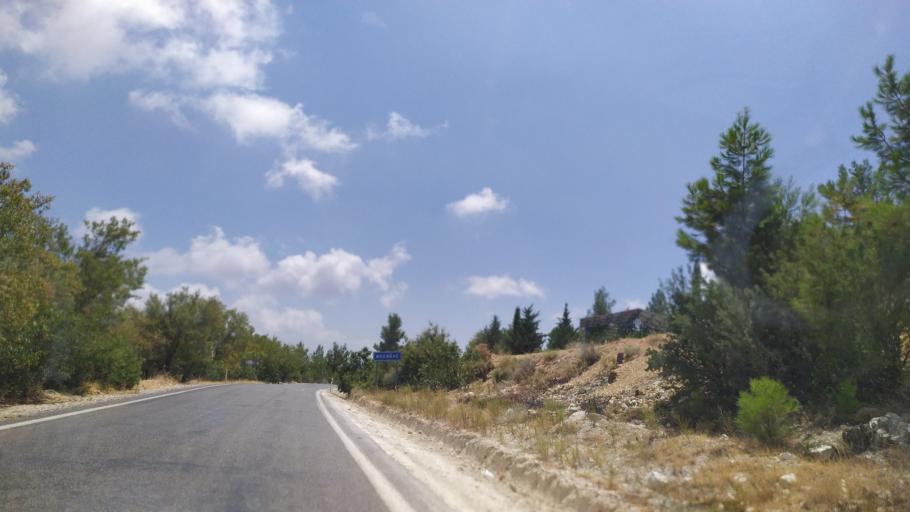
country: TR
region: Mersin
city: Gulnar
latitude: 36.2895
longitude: 33.3813
